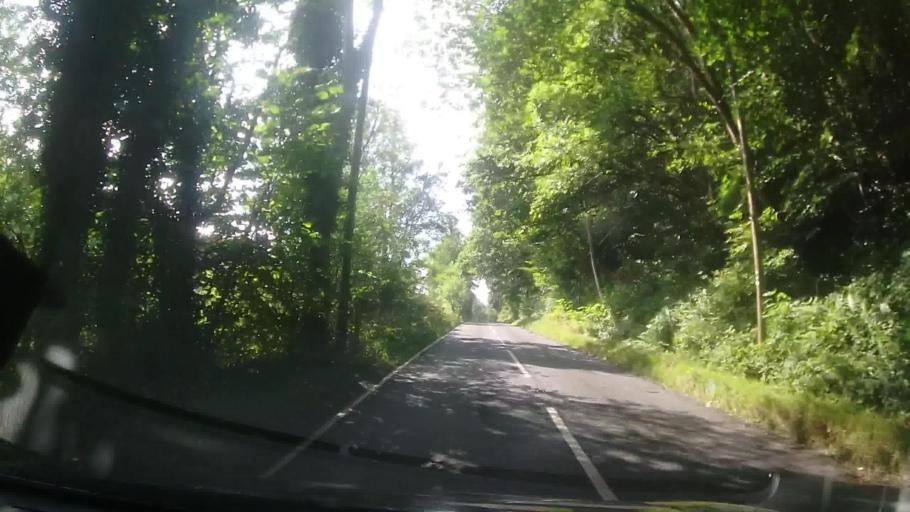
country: GB
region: Wales
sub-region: Sir Powys
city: Knighton
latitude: 52.3525
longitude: -3.0288
